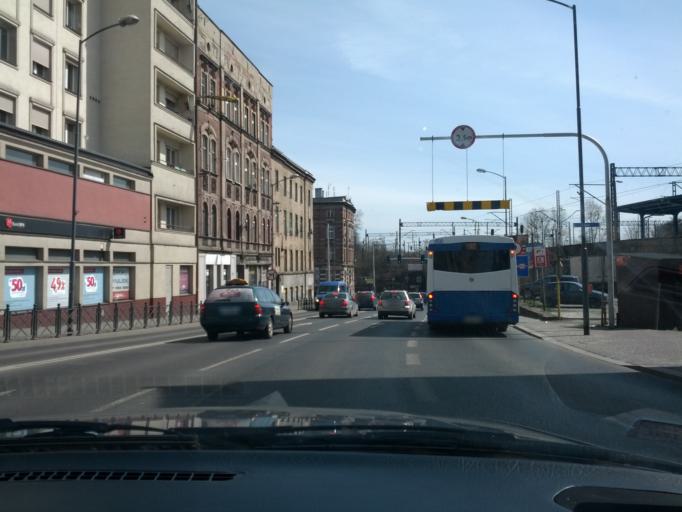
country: PL
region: Silesian Voivodeship
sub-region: Bytom
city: Bytom
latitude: 50.3433
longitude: 18.9158
